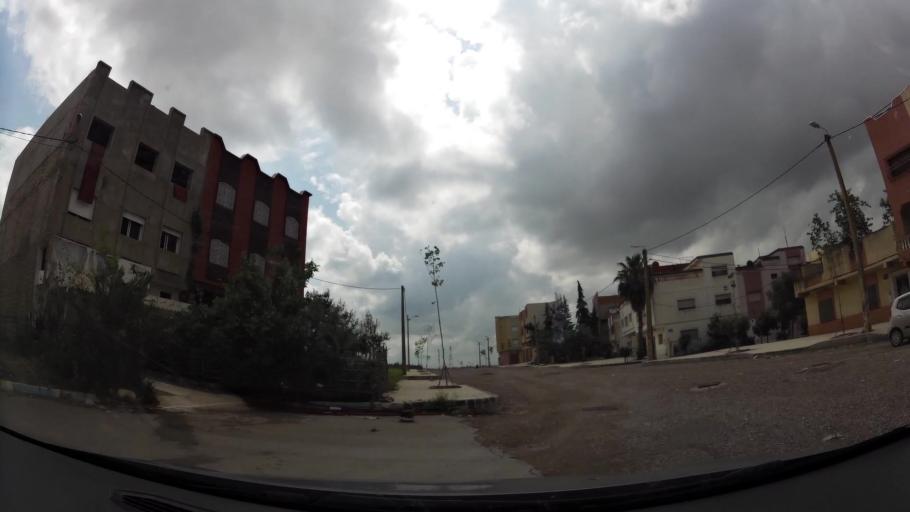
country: MA
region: Rabat-Sale-Zemmour-Zaer
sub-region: Khemisset
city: Tiflet
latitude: 33.8881
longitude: -6.3300
